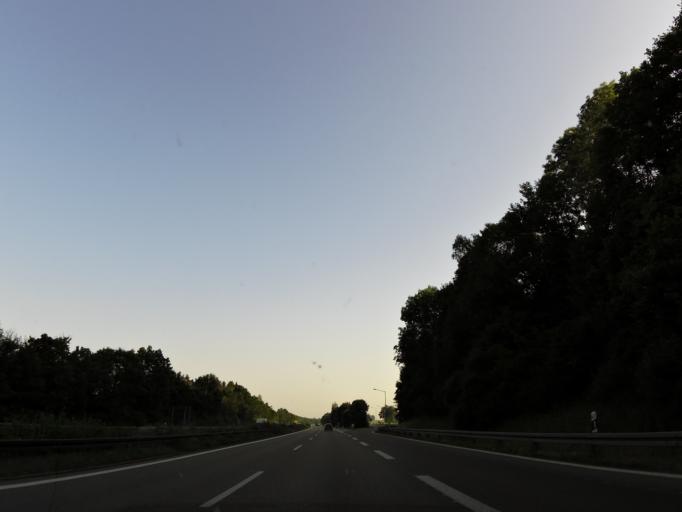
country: DE
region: Bavaria
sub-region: Swabia
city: Illertissen
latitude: 48.2384
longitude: 10.1214
